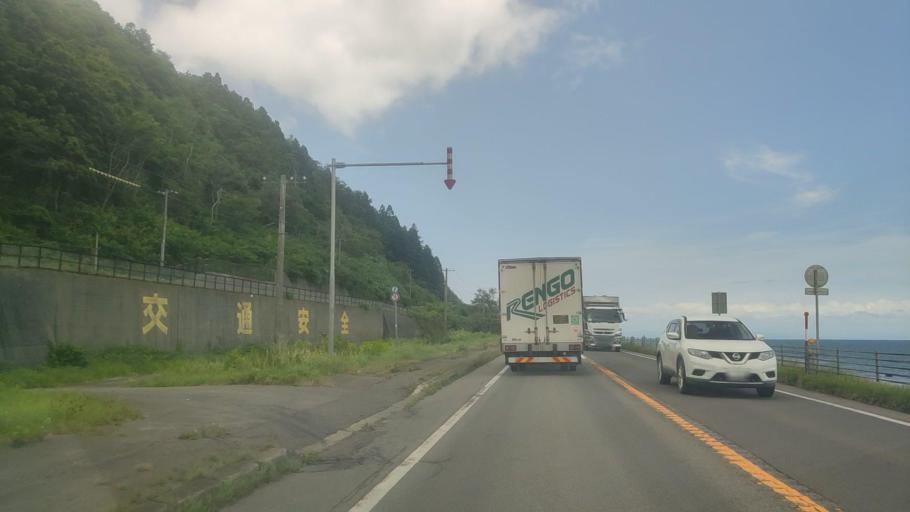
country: JP
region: Hokkaido
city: Nanae
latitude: 42.1480
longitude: 140.4969
